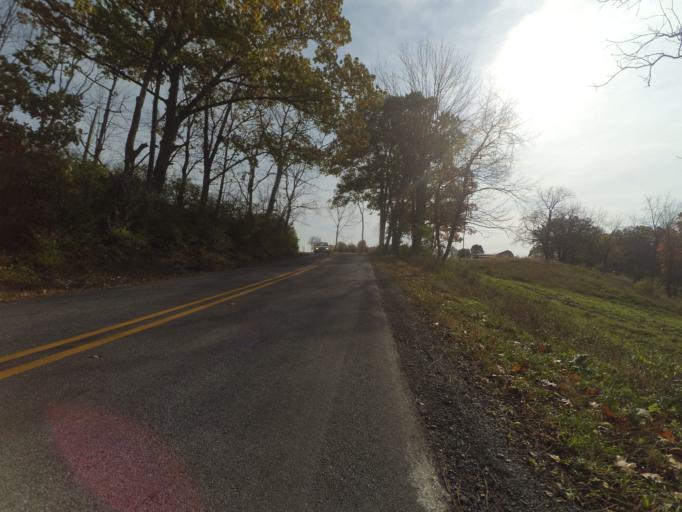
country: US
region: Pennsylvania
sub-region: Centre County
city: Houserville
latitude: 40.8579
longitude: -77.8755
